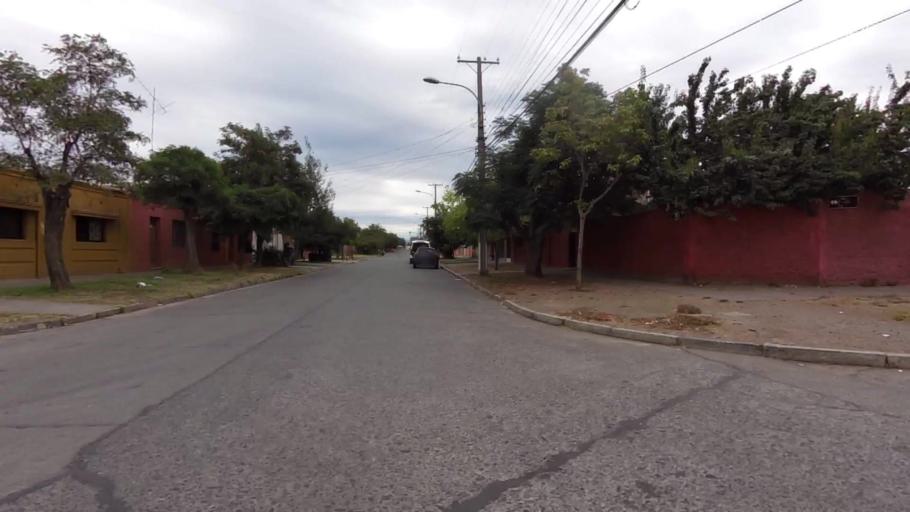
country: CL
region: O'Higgins
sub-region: Provincia de Cachapoal
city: Rancagua
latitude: -34.1630
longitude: -70.7326
